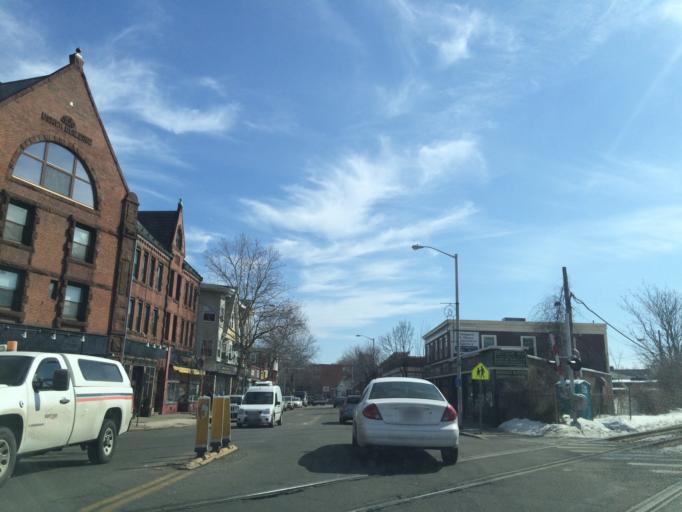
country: US
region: Massachusetts
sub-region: Middlesex County
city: Arlington
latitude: 42.4212
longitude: -71.1327
